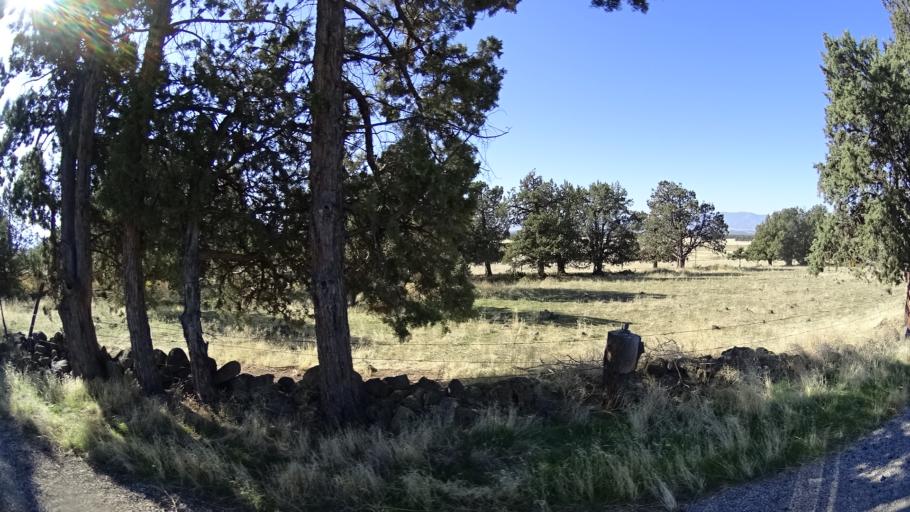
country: US
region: California
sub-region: Siskiyou County
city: Weed
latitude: 41.6232
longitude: -122.3262
